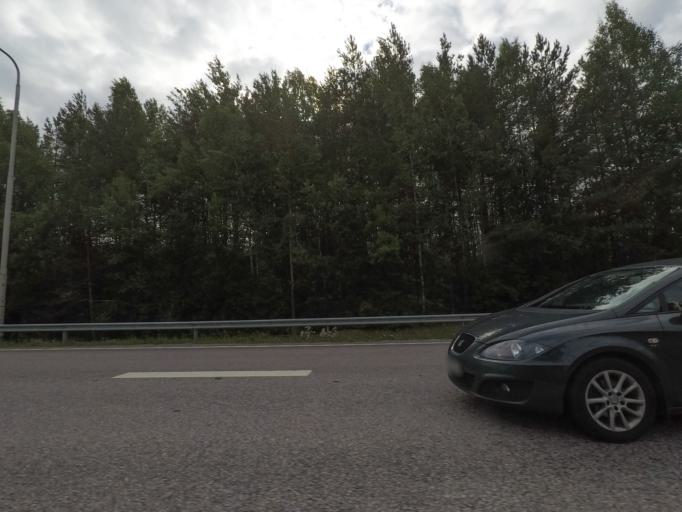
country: FI
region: Uusimaa
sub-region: Helsinki
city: Jaervenpaeae
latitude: 60.4503
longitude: 25.1255
